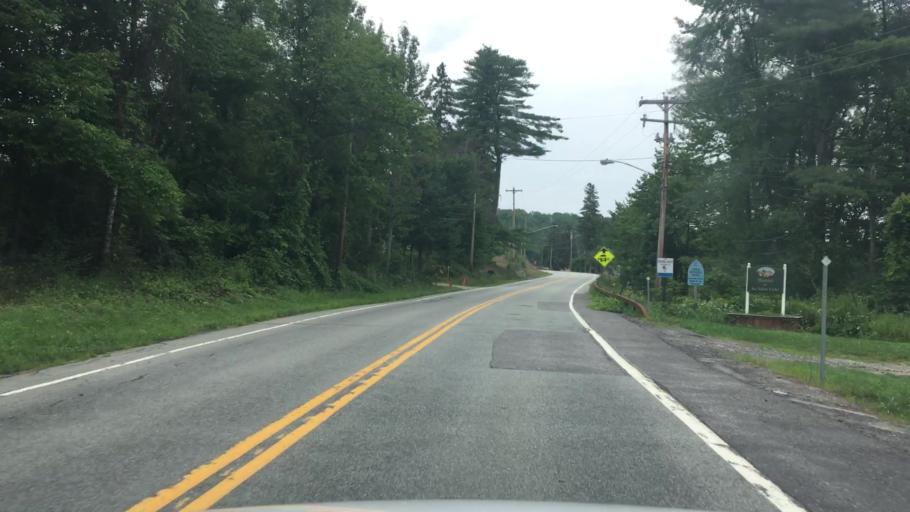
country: US
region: New York
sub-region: Clinton County
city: Peru
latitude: 44.4298
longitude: -73.6799
